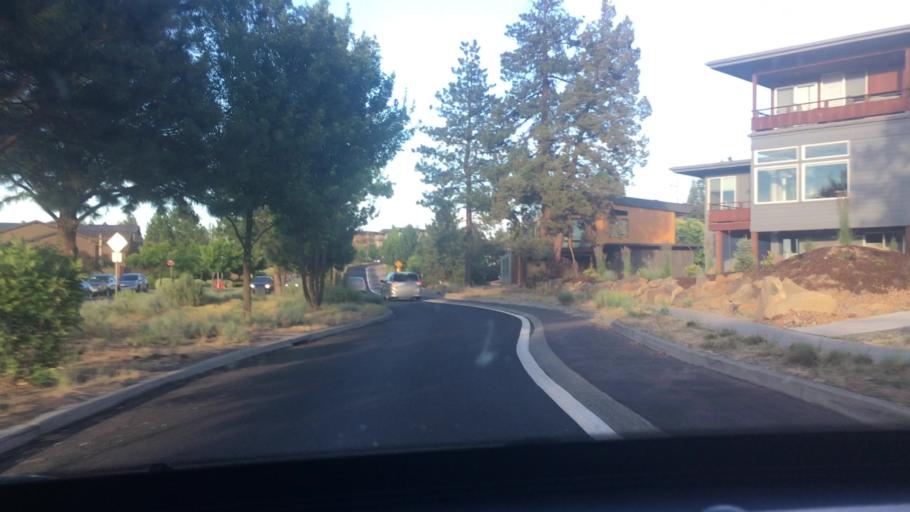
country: US
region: Oregon
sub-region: Deschutes County
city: Bend
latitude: 44.0406
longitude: -121.3205
